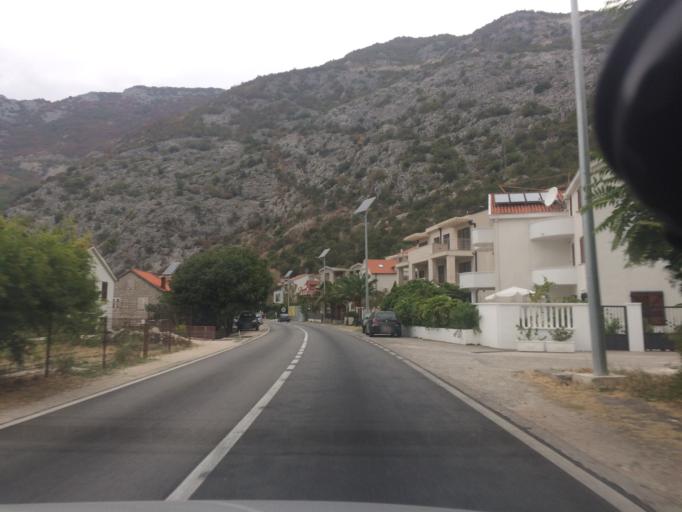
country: ME
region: Kotor
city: Risan
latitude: 42.5170
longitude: 18.6913
